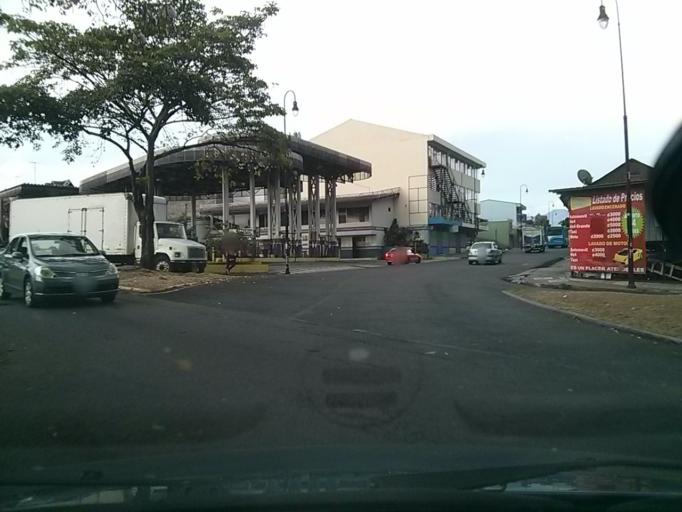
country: CR
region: San Jose
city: San Jose
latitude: 9.9268
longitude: -84.0889
